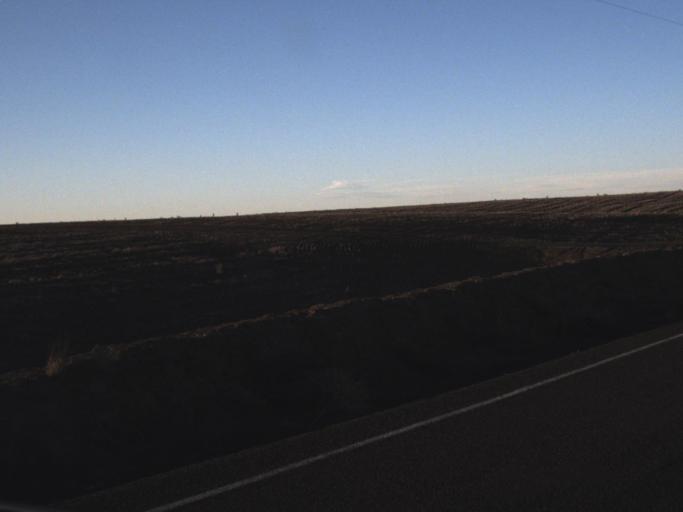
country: US
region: Washington
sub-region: Franklin County
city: Connell
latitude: 46.7506
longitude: -118.5476
